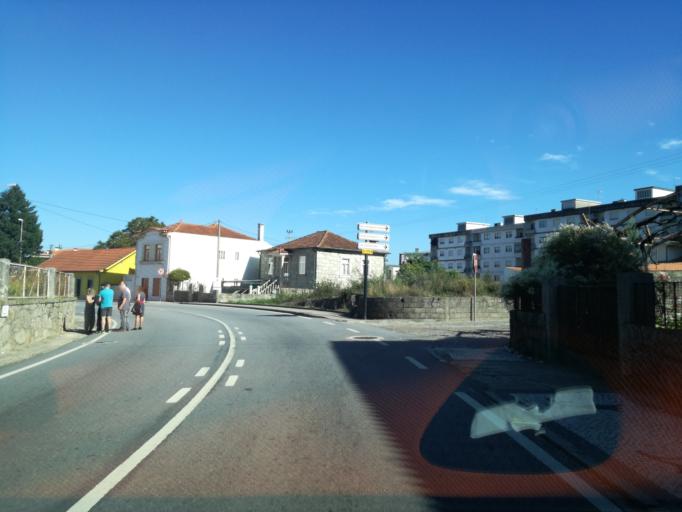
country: PT
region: Porto
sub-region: Trofa
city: Sao Romao do Coronado
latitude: 41.2791
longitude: -8.5560
